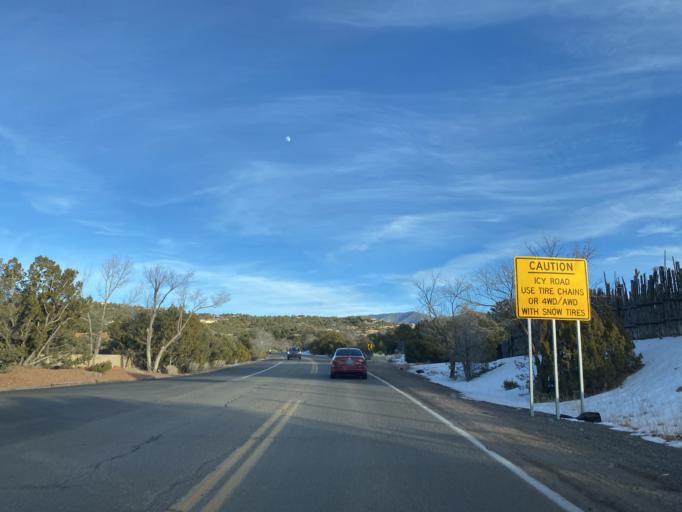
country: US
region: New Mexico
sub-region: Santa Fe County
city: Santa Fe
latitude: 35.6948
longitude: -105.9171
